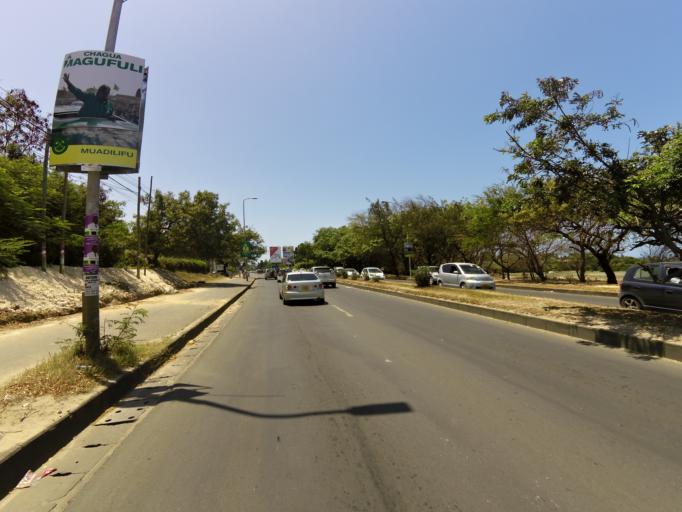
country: TZ
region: Dar es Salaam
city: Magomeni
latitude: -6.7924
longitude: 39.2800
